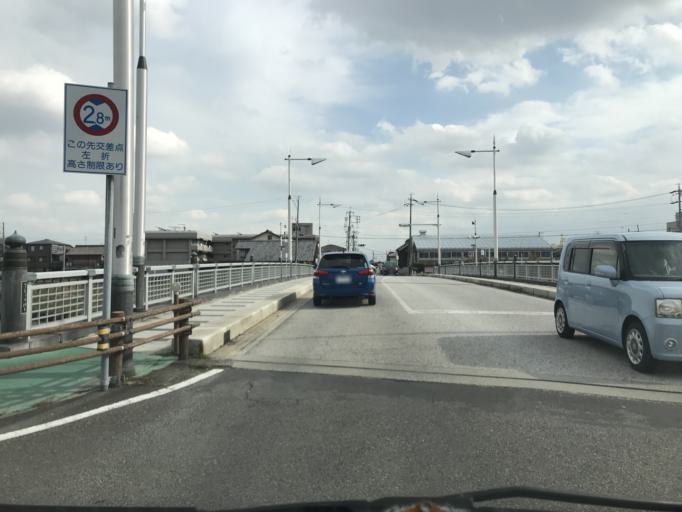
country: JP
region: Aichi
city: Inazawa
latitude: 35.2152
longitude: 136.8399
